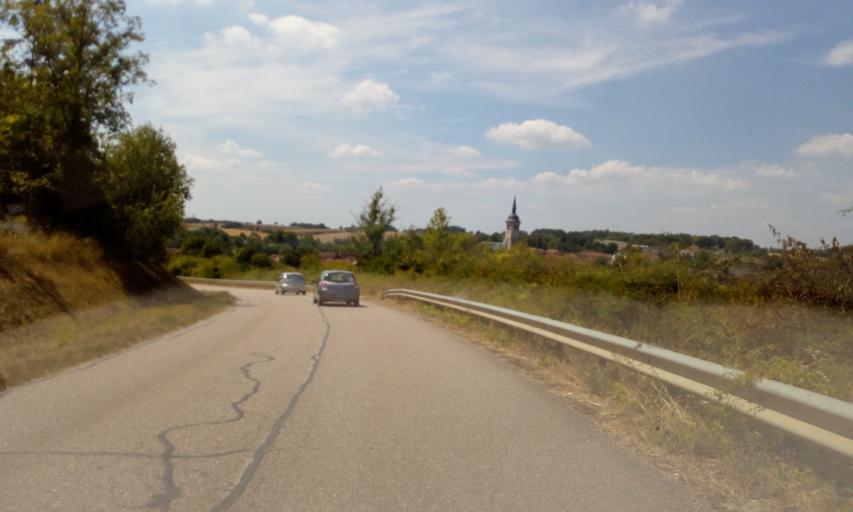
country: FR
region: Lorraine
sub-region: Departement de Meurthe-et-Moselle
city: Pagny-sur-Moselle
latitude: 48.9547
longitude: 5.8714
